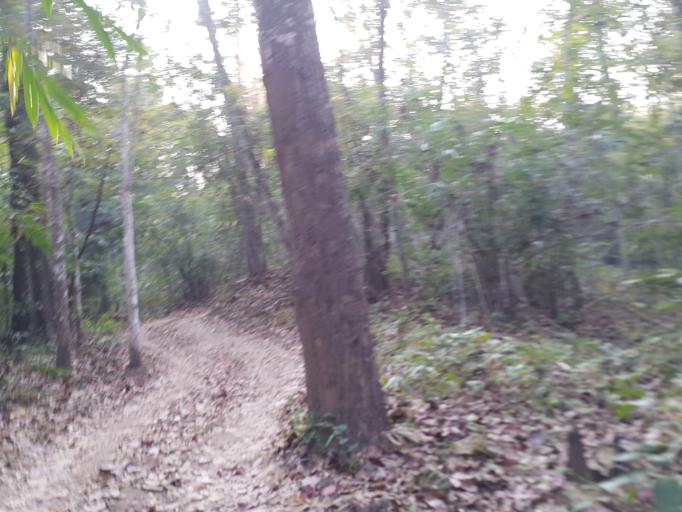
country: TH
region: Lamphun
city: Li
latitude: 17.6174
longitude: 98.8973
